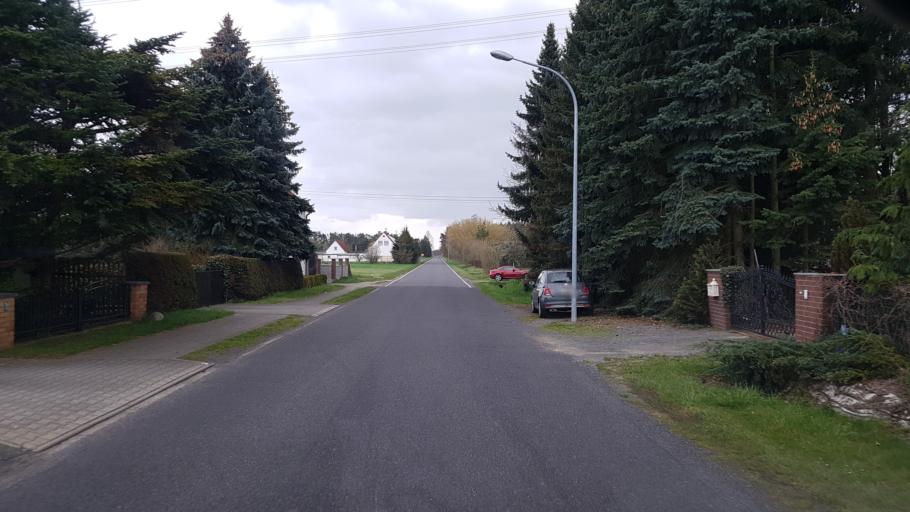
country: DE
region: Brandenburg
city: Finsterwalde
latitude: 51.6573
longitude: 13.7117
